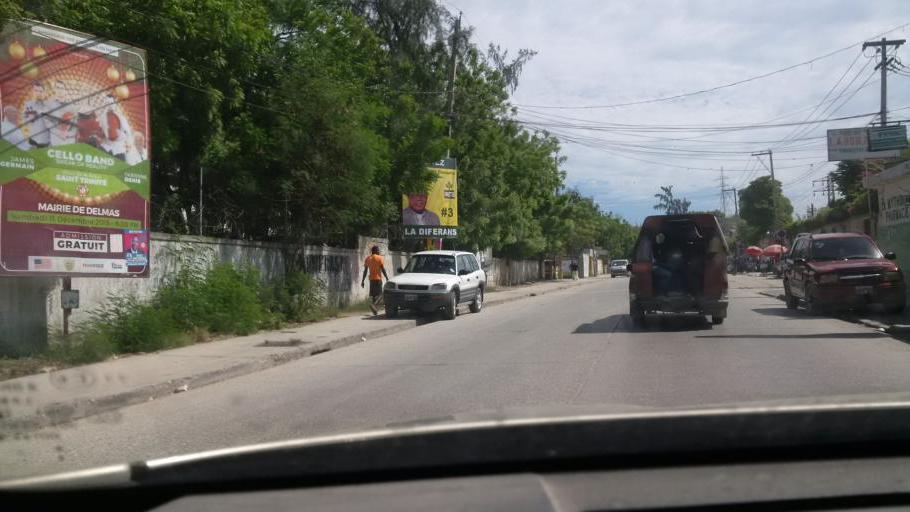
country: HT
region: Ouest
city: Delmas 73
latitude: 18.5564
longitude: -72.2992
